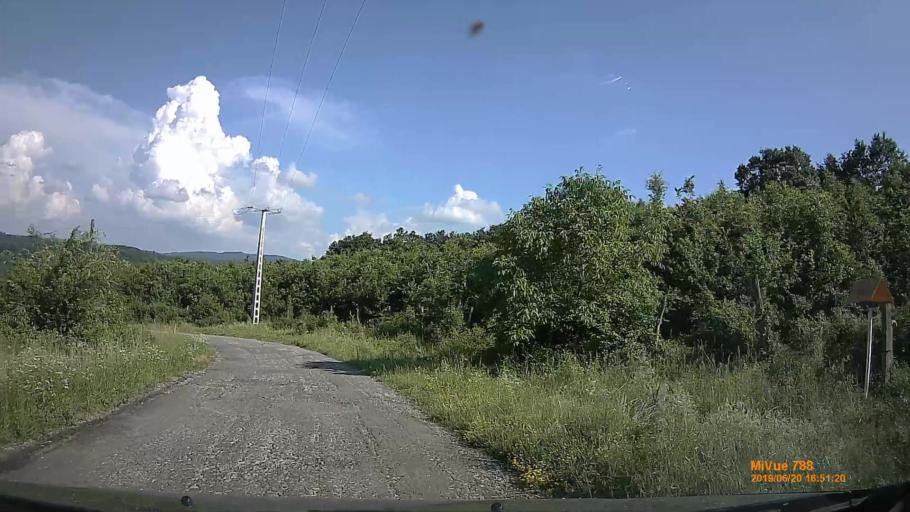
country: HU
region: Baranya
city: Buekkoesd
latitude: 46.1545
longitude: 18.0500
